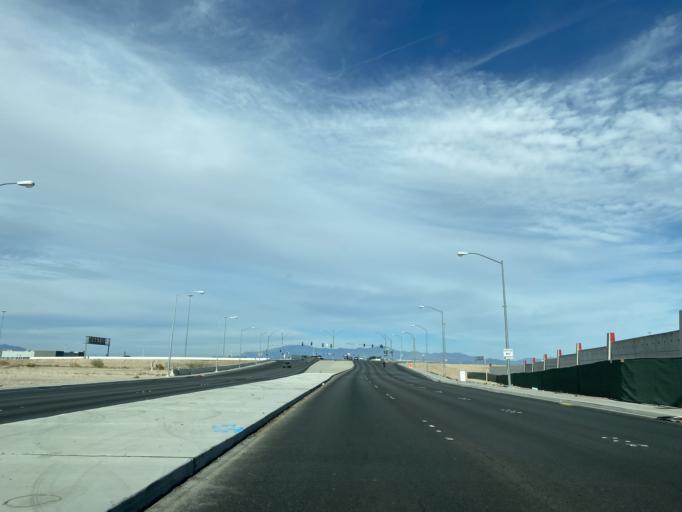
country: US
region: Nevada
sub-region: Clark County
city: Enterprise
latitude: 36.0637
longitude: -115.2246
